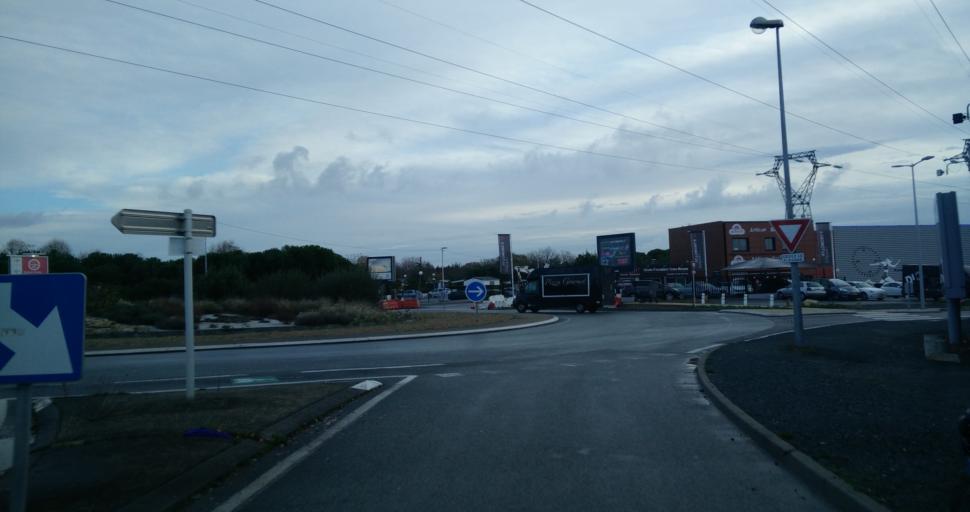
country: FR
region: Poitou-Charentes
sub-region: Departement de la Charente-Maritime
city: Puilboreau
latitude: 46.1774
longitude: -1.1166
